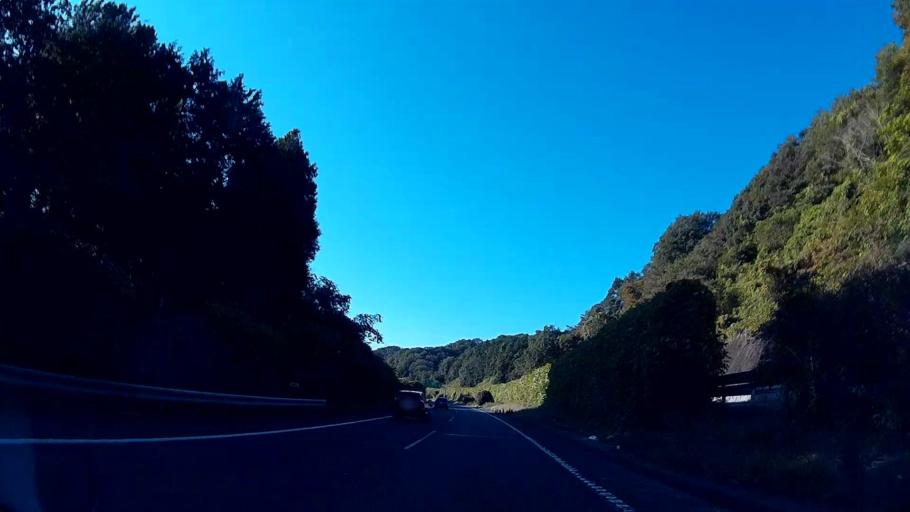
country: JP
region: Tokyo
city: Hachioji
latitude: 35.6514
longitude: 139.2665
